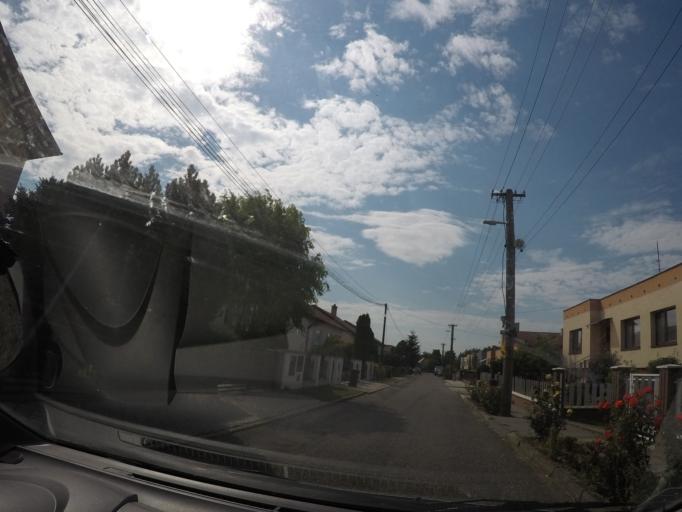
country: SK
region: Nitriansky
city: Levice
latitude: 48.2774
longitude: 18.6314
